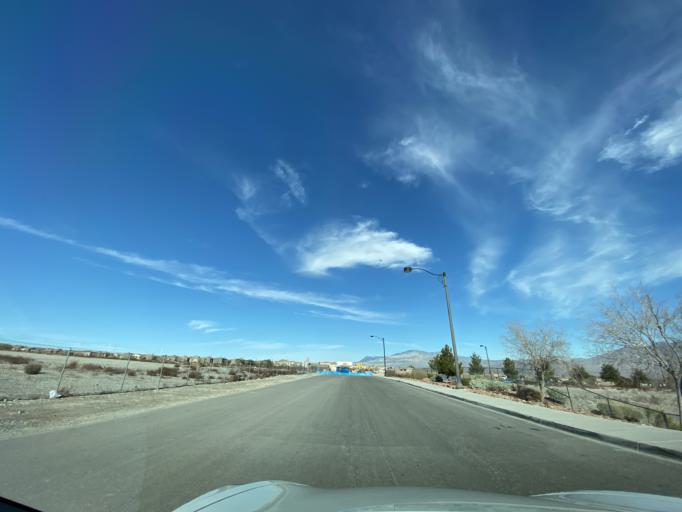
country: US
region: Nevada
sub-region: Clark County
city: Summerlin South
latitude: 36.2967
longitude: -115.3230
